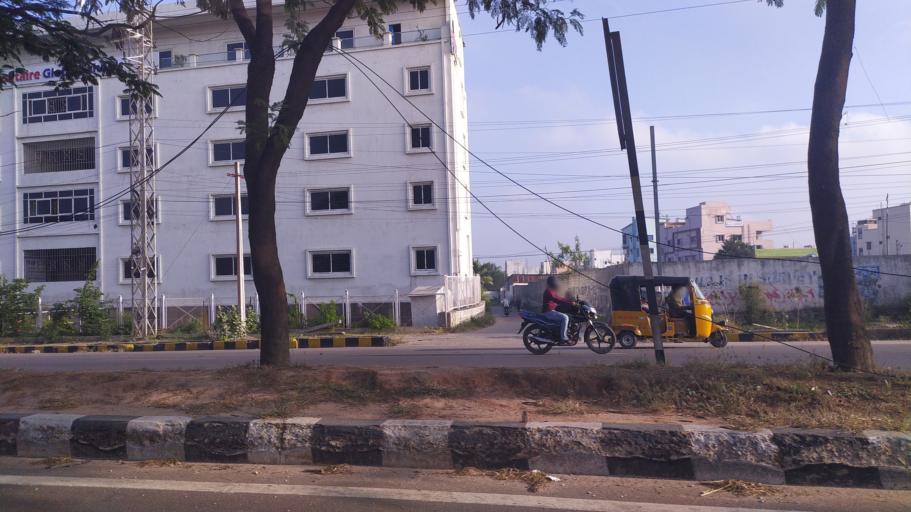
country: IN
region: Telangana
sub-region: Rangareddi
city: Balapur
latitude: 17.3163
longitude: 78.4407
